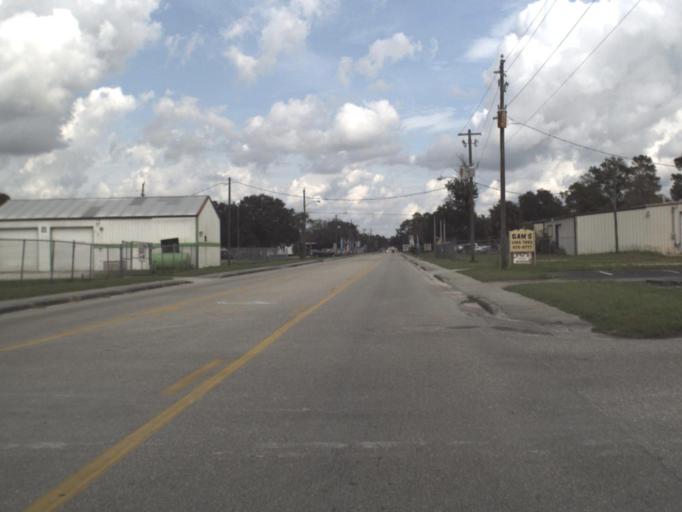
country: US
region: Florida
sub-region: Hendry County
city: LaBelle
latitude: 26.7517
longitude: -81.4373
